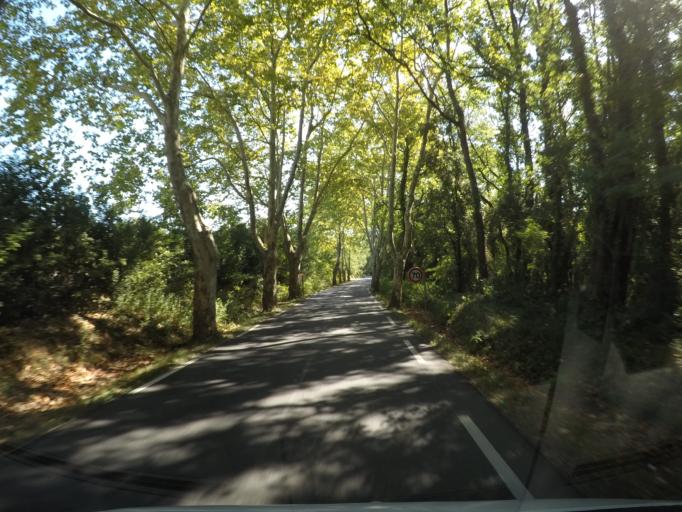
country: FR
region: Languedoc-Roussillon
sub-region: Departement du Gard
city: Montaren-et-Saint-Mediers
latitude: 44.0012
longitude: 4.3817
